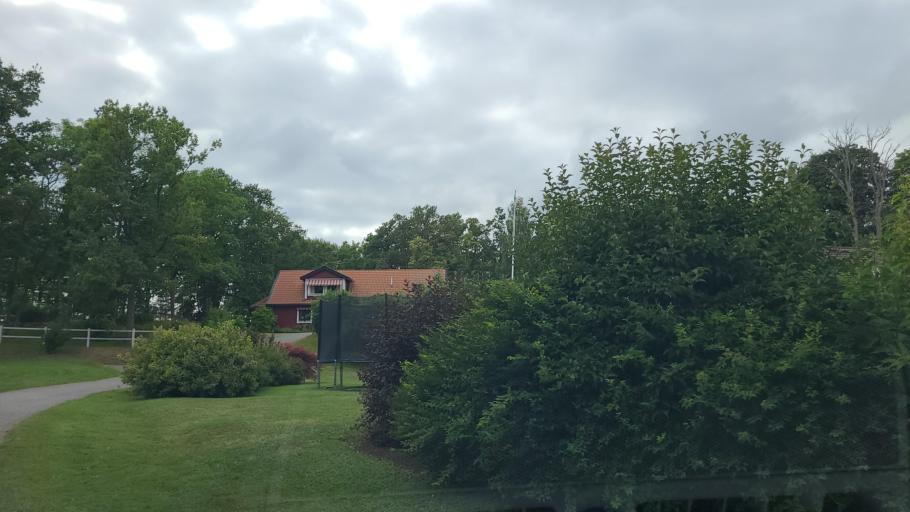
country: SE
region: Stockholm
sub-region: Upplands-Bro Kommun
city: Bro
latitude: 59.4532
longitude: 17.5813
